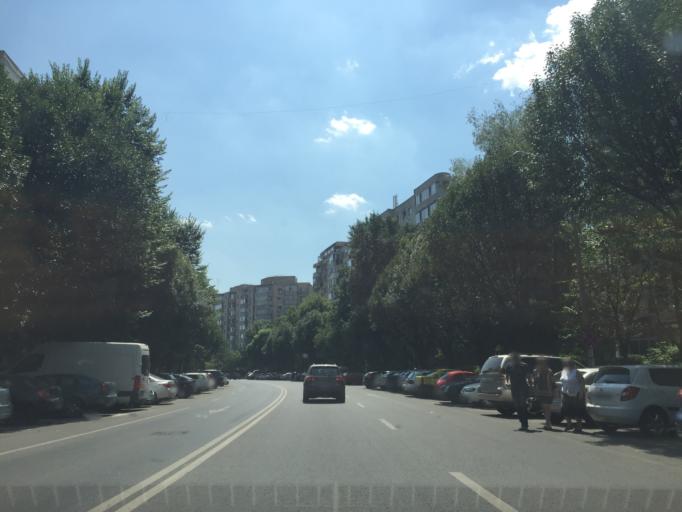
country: RO
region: Bucuresti
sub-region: Municipiul Bucuresti
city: Bucharest
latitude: 44.4111
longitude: 26.1150
